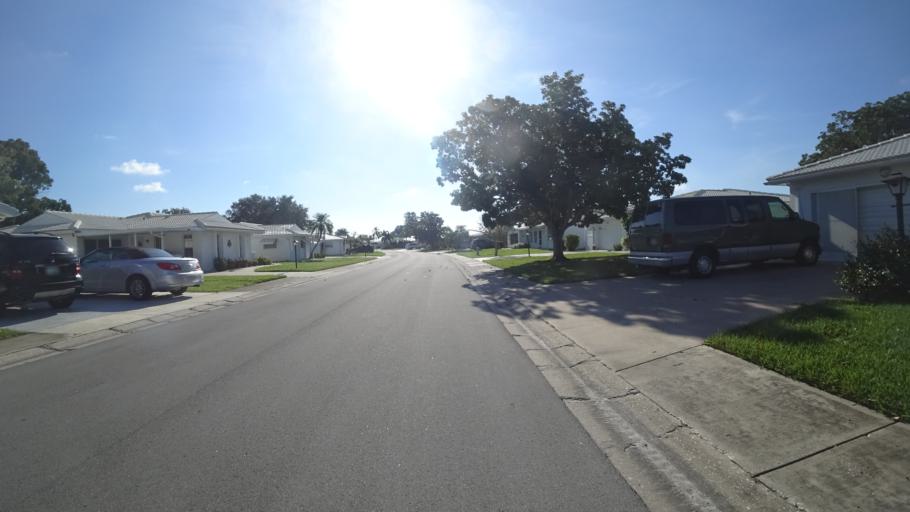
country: US
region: Florida
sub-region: Manatee County
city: Ellenton
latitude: 27.4958
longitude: -82.5133
